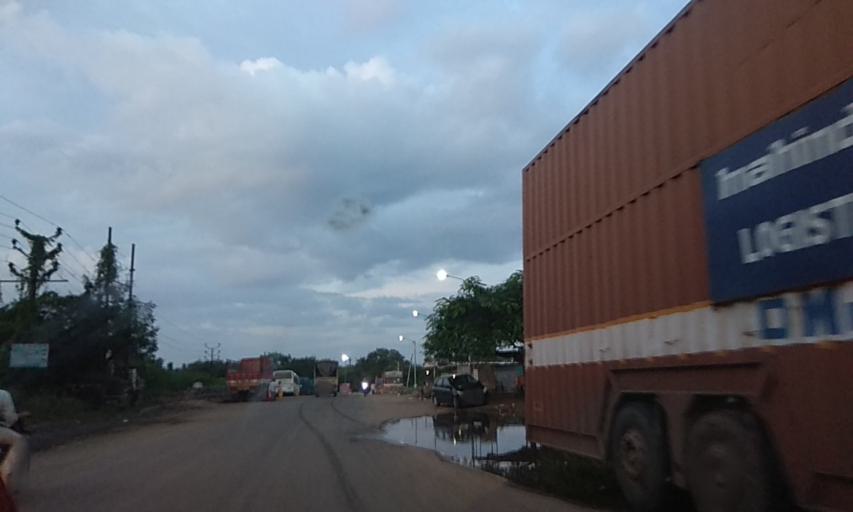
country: IN
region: Maharashtra
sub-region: Pune Division
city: Pune
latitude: 18.5182
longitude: 73.9154
